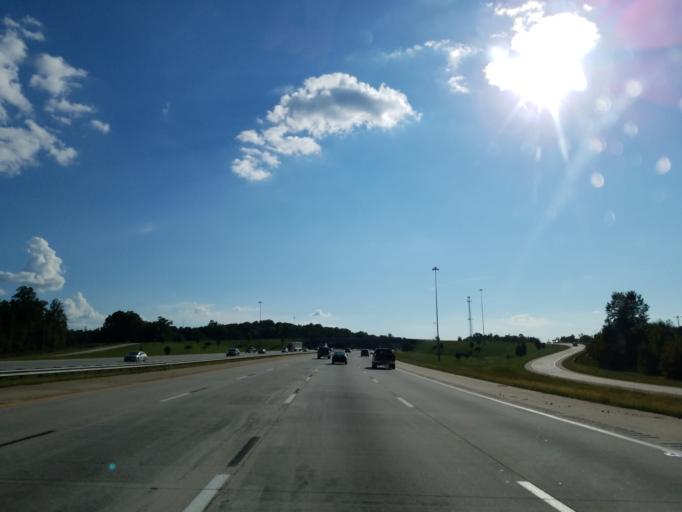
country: US
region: North Carolina
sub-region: Rowan County
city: East Spencer
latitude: 35.6804
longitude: -80.4109
